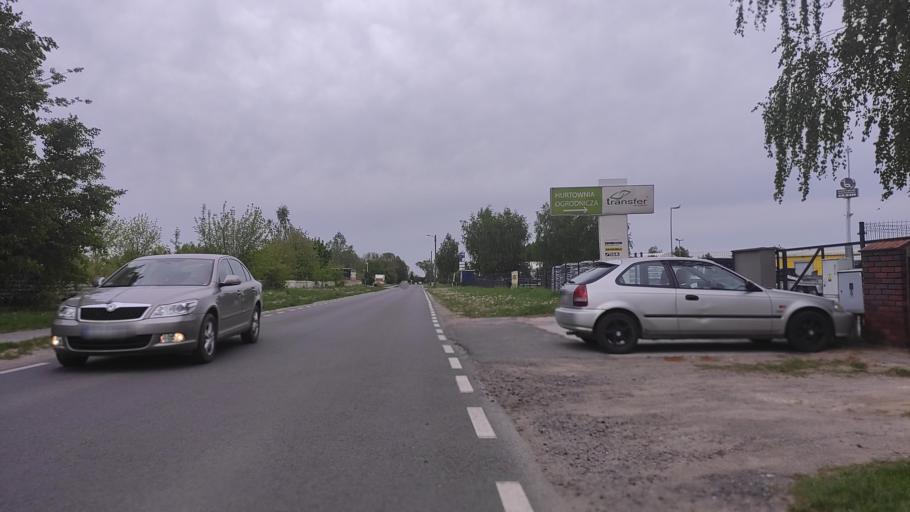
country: PL
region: Greater Poland Voivodeship
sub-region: Powiat poznanski
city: Swarzedz
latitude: 52.4095
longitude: 17.1065
